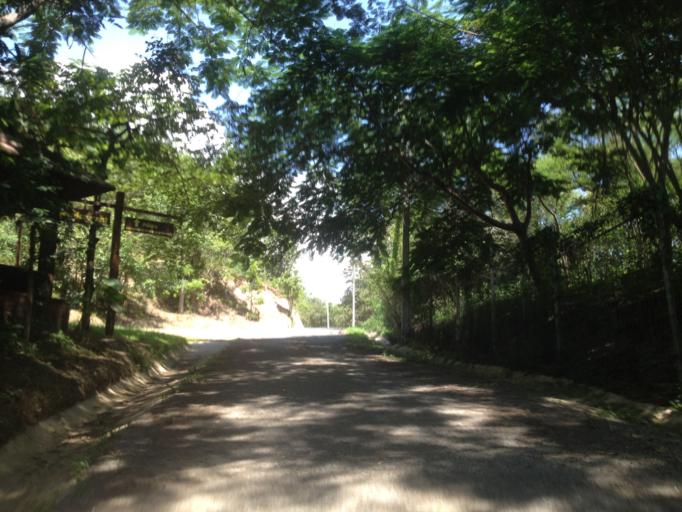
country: TH
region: Chiang Mai
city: Hang Dong
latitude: 18.7378
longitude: 98.9121
